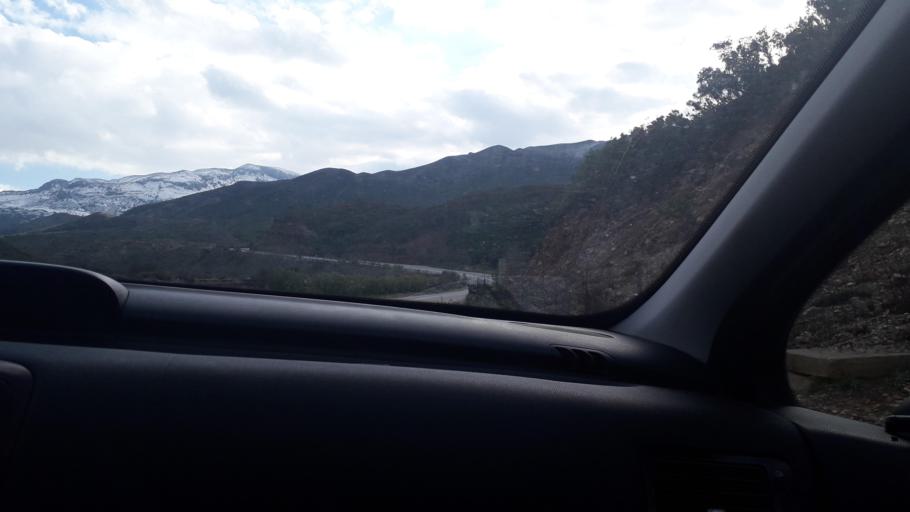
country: GR
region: Crete
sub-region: Nomos Rethymnis
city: Agia Foteini
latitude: 35.2796
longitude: 24.5626
